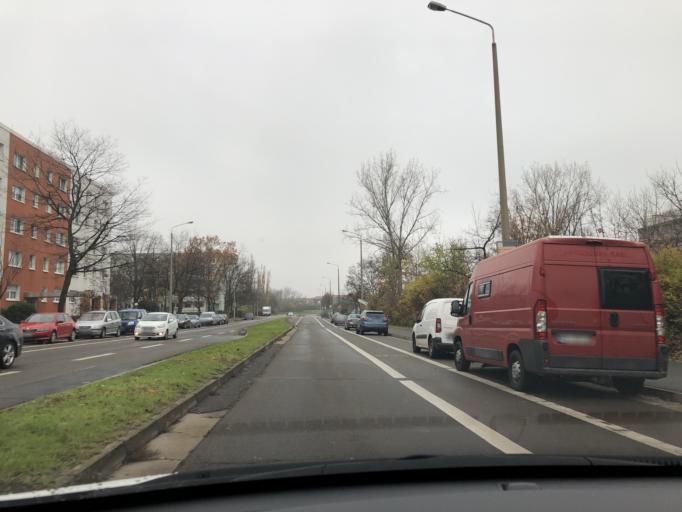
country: DE
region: Saxony-Anhalt
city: Halle Neustadt
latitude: 51.4842
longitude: 11.9282
